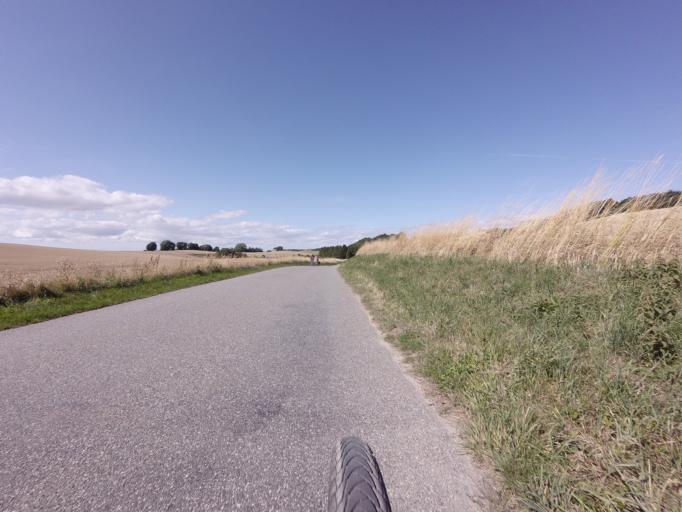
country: DK
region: Zealand
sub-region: Vordingborg Kommune
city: Stege
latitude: 54.9967
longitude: 12.5213
